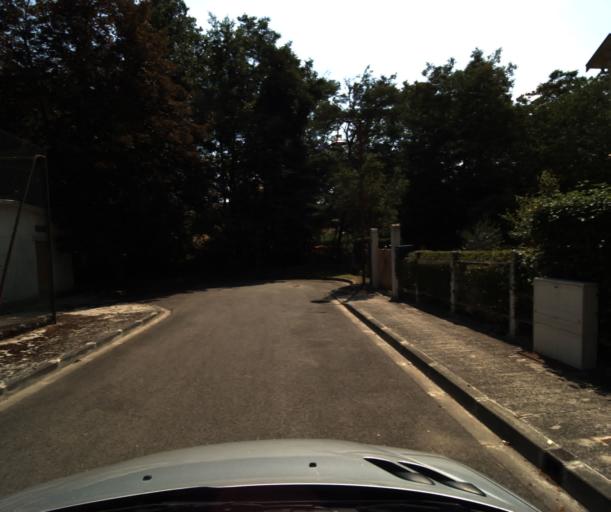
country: FR
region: Midi-Pyrenees
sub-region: Departement de la Haute-Garonne
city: Saint-Lys
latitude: 43.5171
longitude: 1.1739
